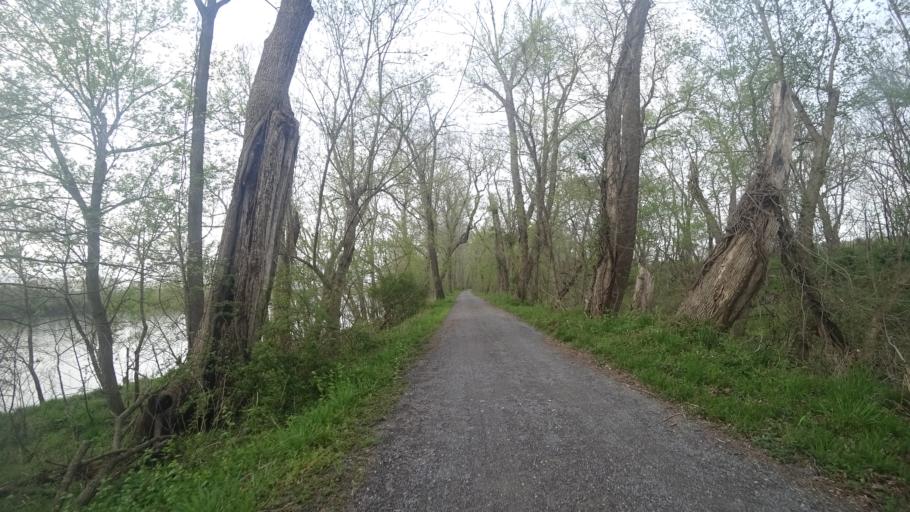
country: US
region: Virginia
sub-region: Loudoun County
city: Leesburg
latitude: 39.1307
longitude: -77.5148
